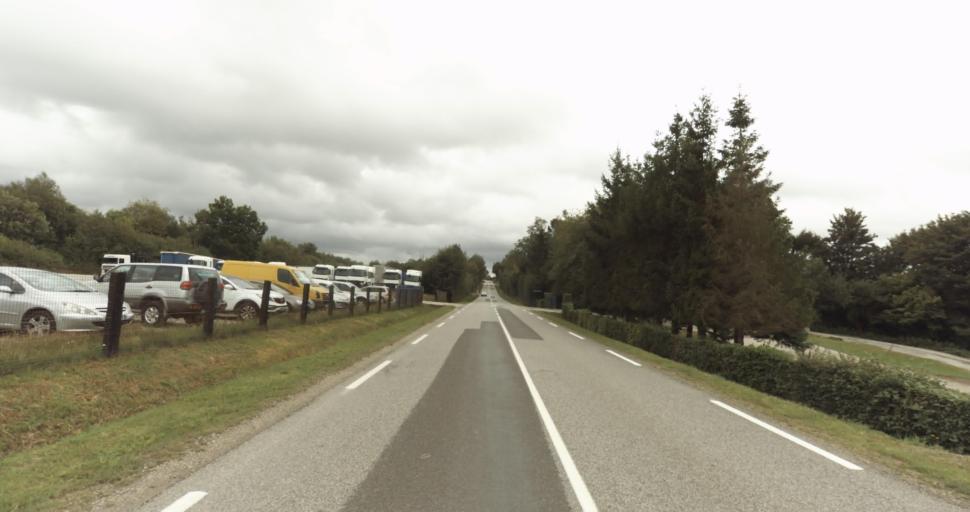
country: FR
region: Lower Normandy
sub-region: Departement de l'Orne
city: Sainte-Gauburge-Sainte-Colombe
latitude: 48.7037
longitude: 0.4378
